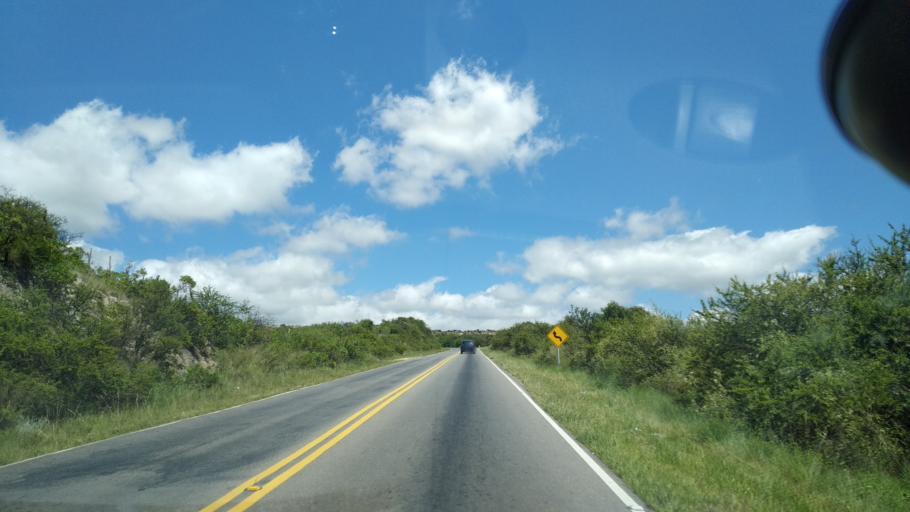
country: AR
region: Cordoba
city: Villa Cura Brochero
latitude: -31.6985
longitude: -65.0543
